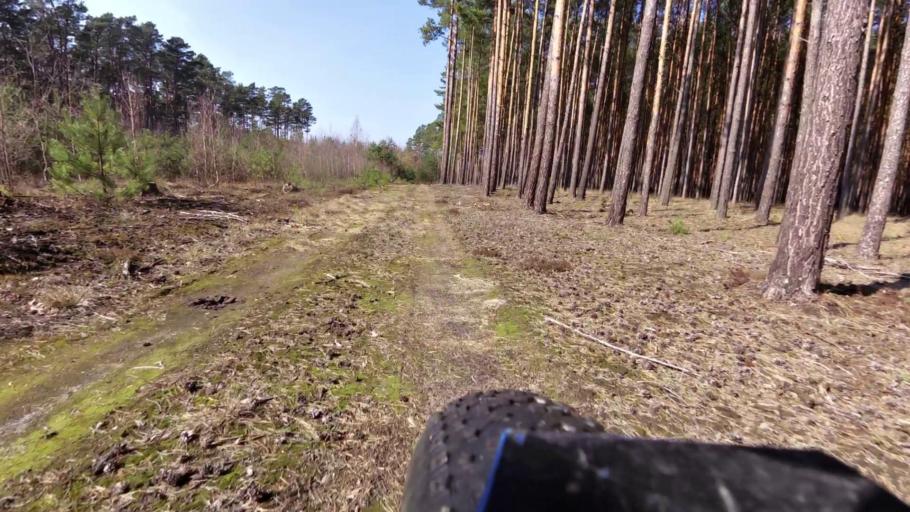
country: PL
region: Lubusz
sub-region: Powiat slubicki
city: Cybinka
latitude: 52.2105
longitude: 14.9156
